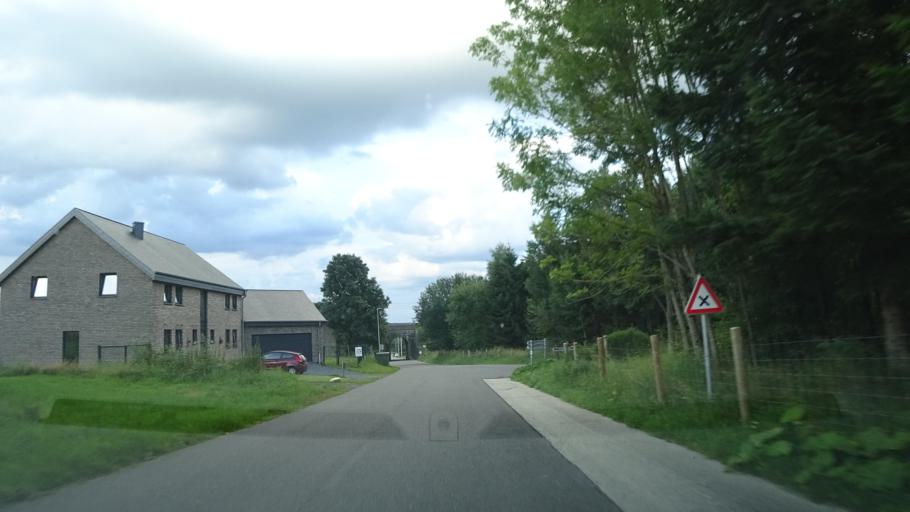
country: BE
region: Wallonia
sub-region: Province du Luxembourg
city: Bertrix
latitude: 49.8144
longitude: 5.3140
